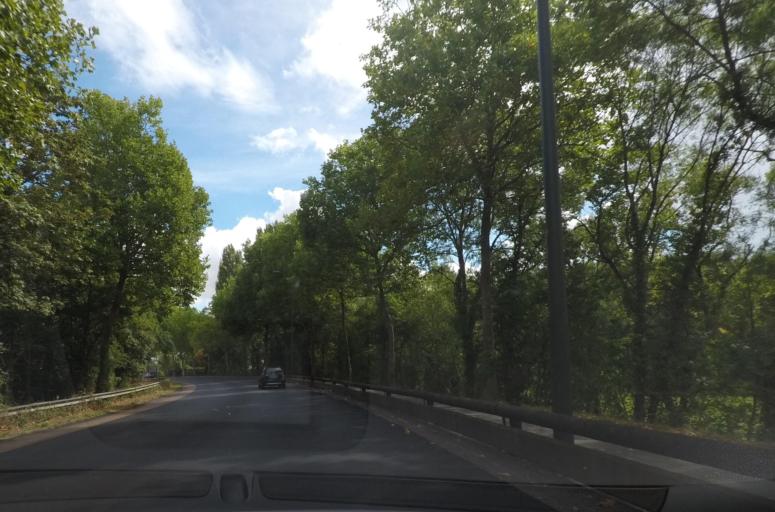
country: FR
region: Pays de la Loire
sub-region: Departement de la Sarthe
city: La Fleche
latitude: 47.6968
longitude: -0.0637
